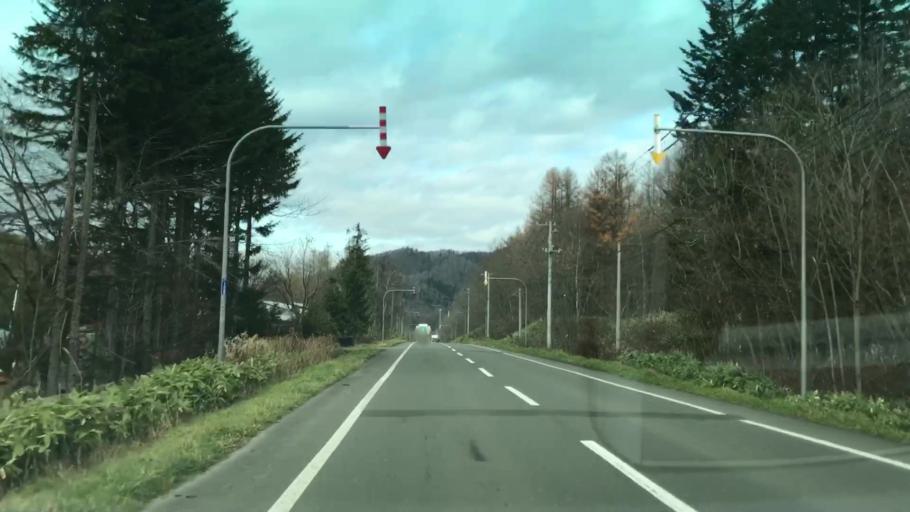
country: JP
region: Hokkaido
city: Shimo-furano
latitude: 42.9401
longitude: 142.4447
